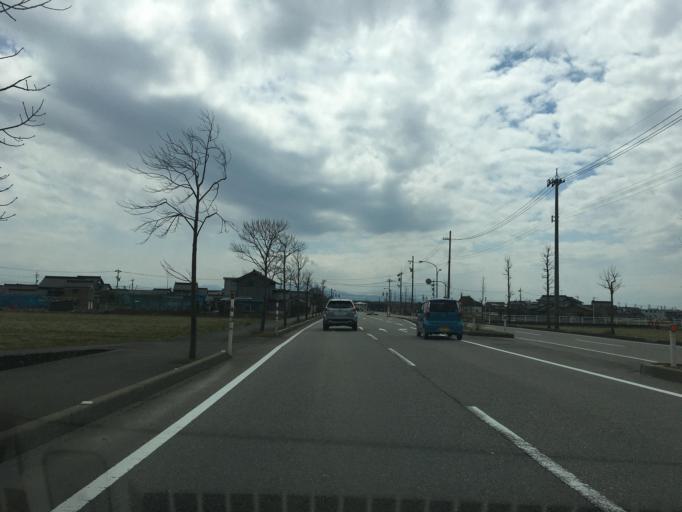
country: JP
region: Toyama
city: Kuragaki-kosugi
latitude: 36.7249
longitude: 137.1215
